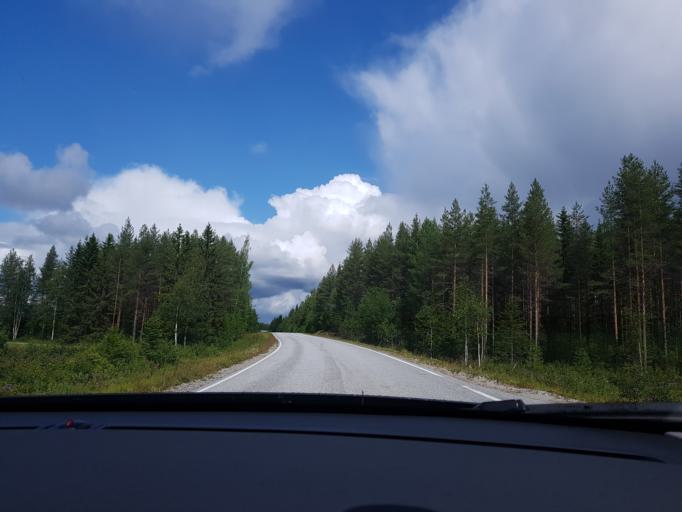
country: FI
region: Kainuu
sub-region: Kehys-Kainuu
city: Kuhmo
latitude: 64.4267
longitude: 29.4989
